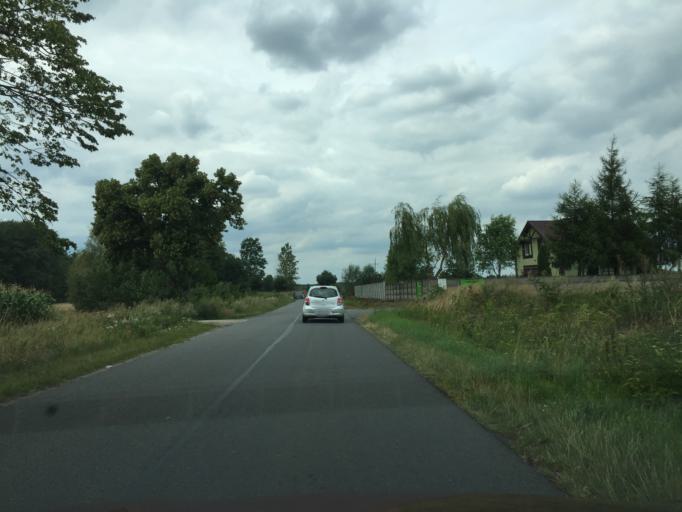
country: PL
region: Greater Poland Voivodeship
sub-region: Powiat kaliski
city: Stawiszyn
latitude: 51.9470
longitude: 18.1820
